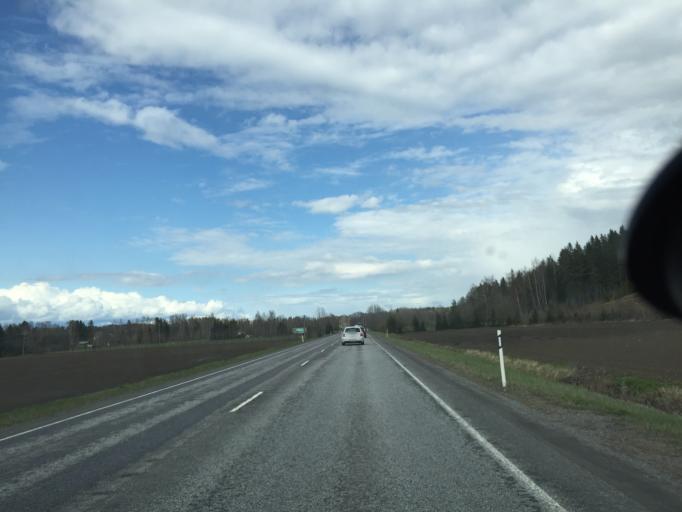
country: FI
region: Uusimaa
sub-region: Helsinki
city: Lohja
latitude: 60.2002
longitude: 24.0148
